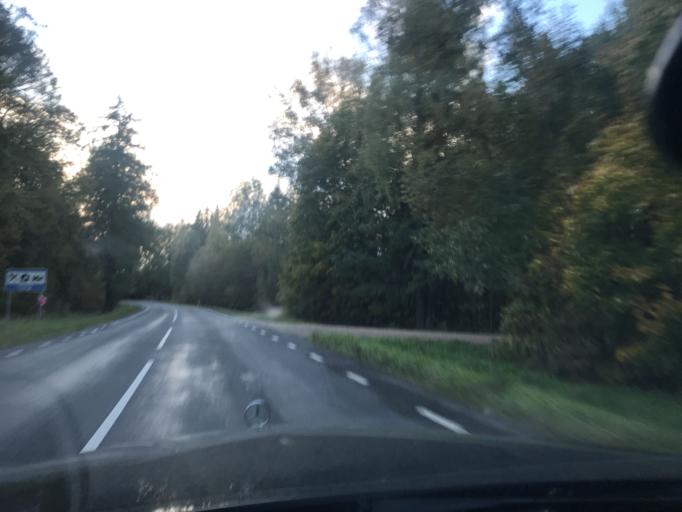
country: EE
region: Vorumaa
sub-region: Antsla vald
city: Vana-Antsla
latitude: 57.8831
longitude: 26.5652
